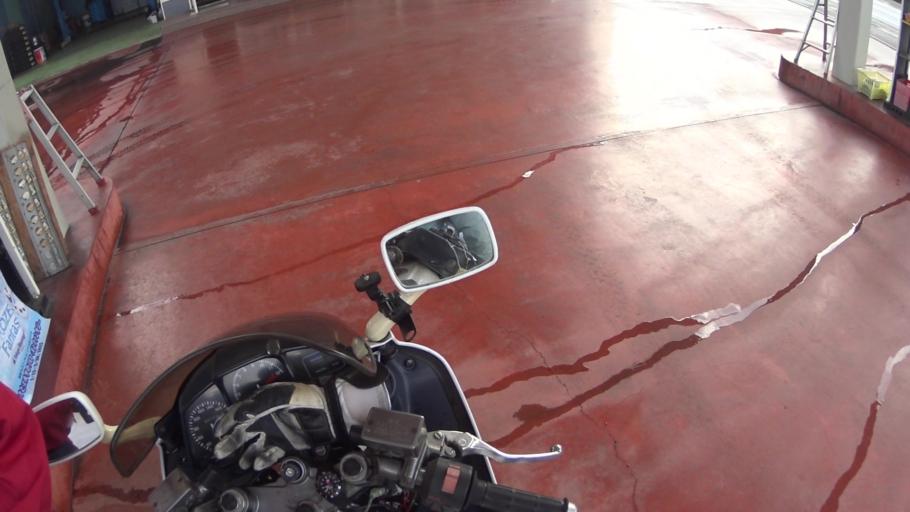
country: JP
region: Kyoto
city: Ayabe
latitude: 35.3054
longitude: 135.2197
